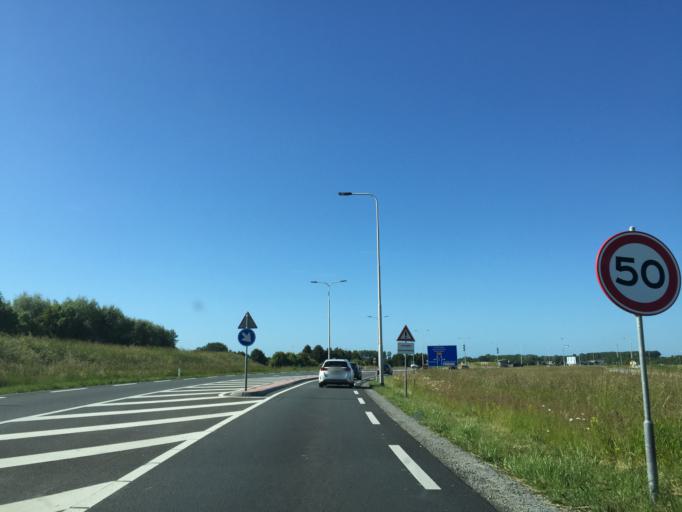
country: NL
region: South Holland
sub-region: Gemeente Goeree-Overflakkee
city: Ouddorp
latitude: 51.8063
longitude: 3.9452
